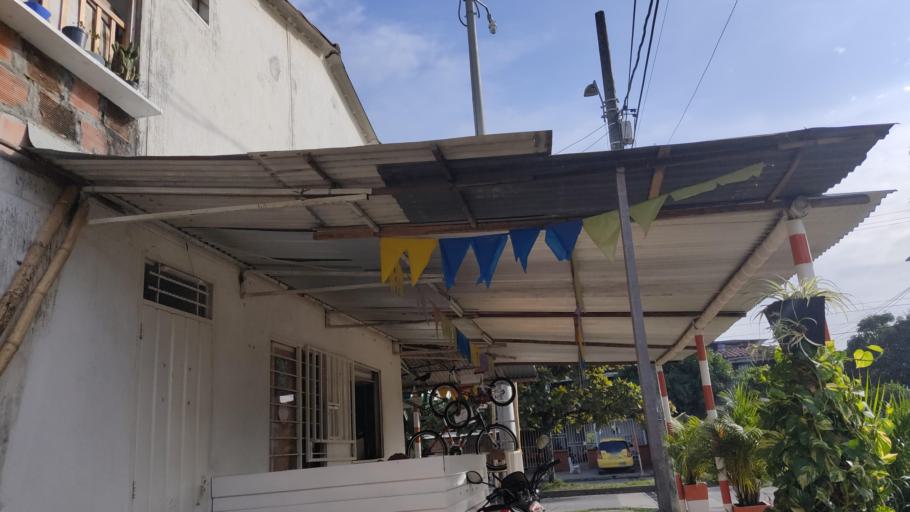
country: CO
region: Valle del Cauca
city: Jamundi
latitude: 3.2396
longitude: -76.5121
